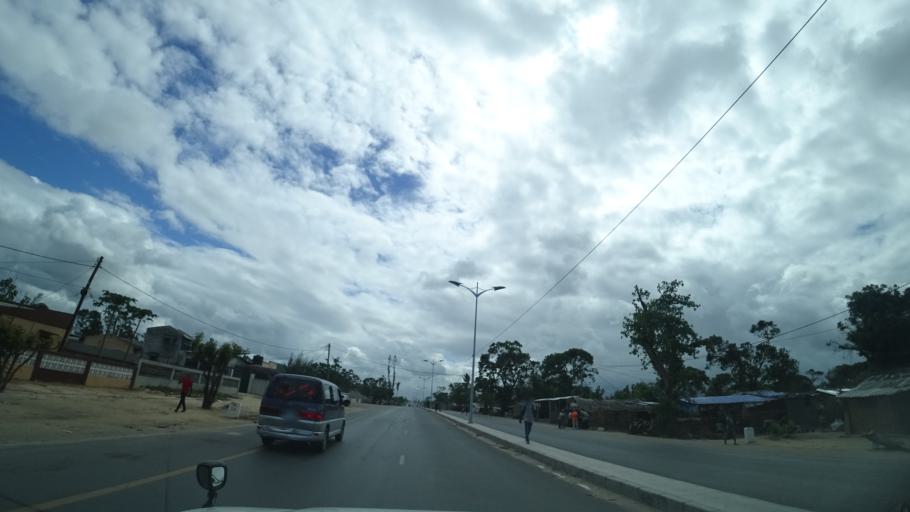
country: MZ
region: Sofala
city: Dondo
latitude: -19.6086
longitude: 34.7437
